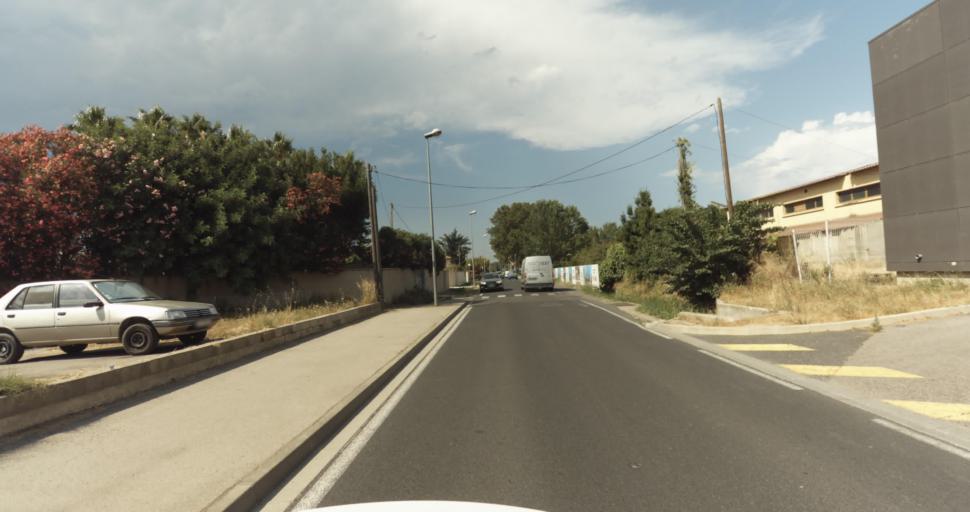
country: FR
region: Languedoc-Roussillon
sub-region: Departement des Pyrenees-Orientales
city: Elne
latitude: 42.6053
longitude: 2.9740
